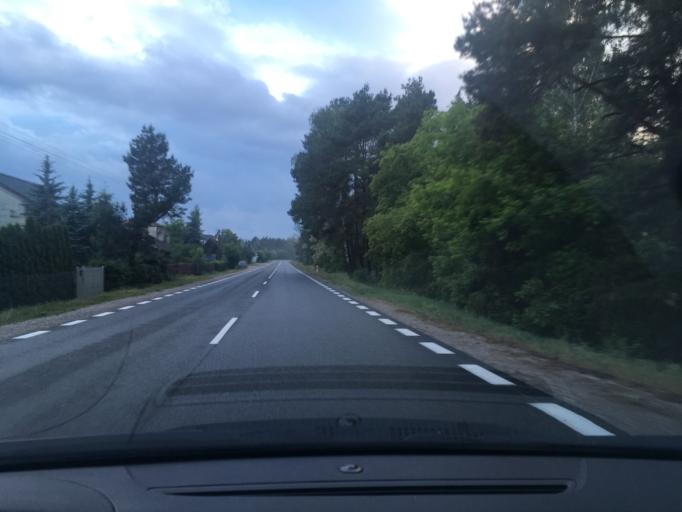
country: PL
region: Masovian Voivodeship
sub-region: Powiat garwolinski
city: Wilga
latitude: 51.7905
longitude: 21.4414
